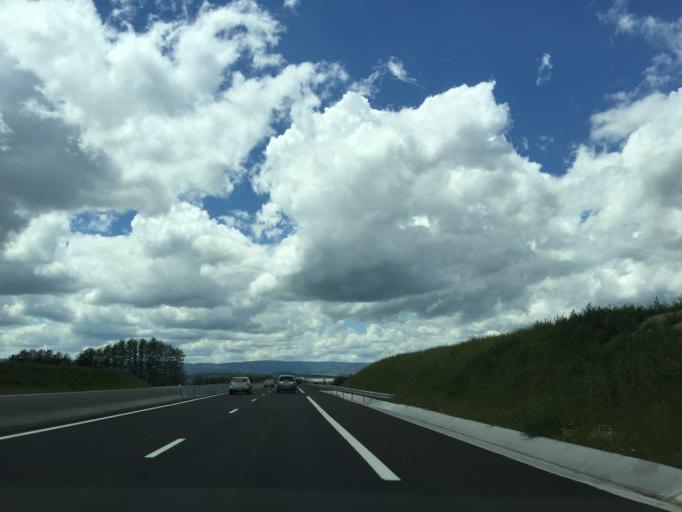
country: FR
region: Rhone-Alpes
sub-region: Departement de la Loire
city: Bonson
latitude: 45.5139
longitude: 4.2080
